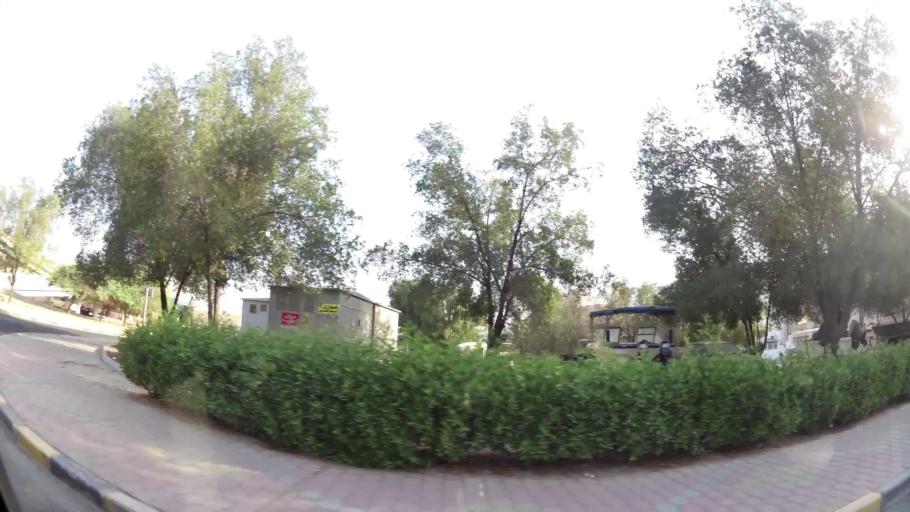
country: KW
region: Al Asimah
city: Ad Dasmah
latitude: 29.3551
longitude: 48.0059
